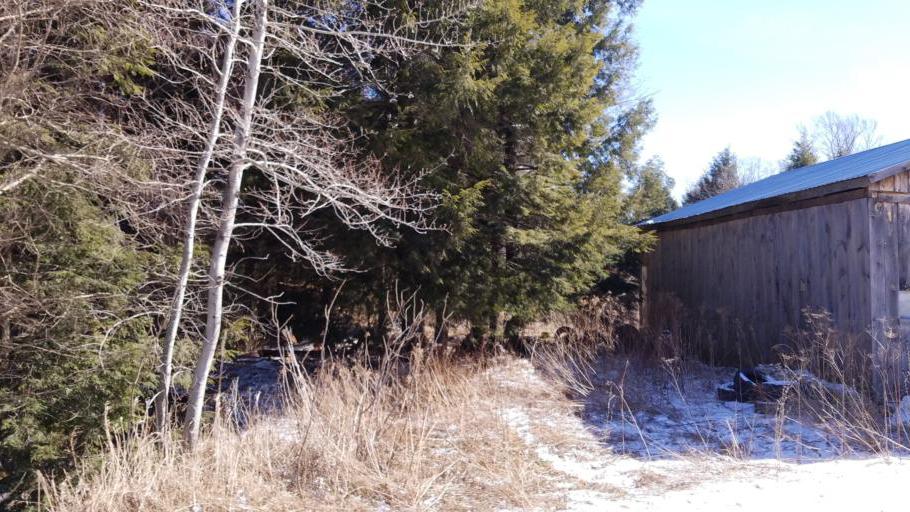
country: US
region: New York
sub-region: Allegany County
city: Andover
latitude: 42.0117
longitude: -77.7726
